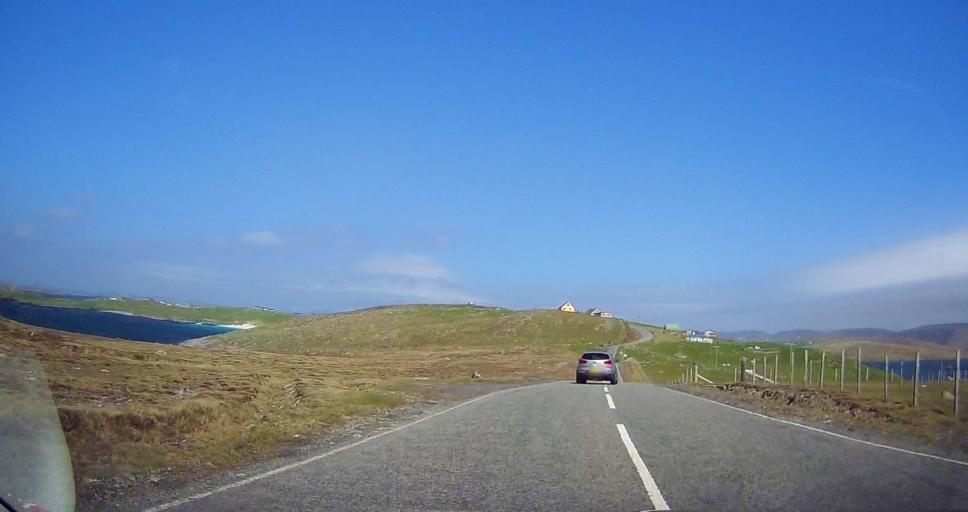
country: GB
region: Scotland
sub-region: Shetland Islands
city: Sandwick
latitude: 60.0920
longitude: -1.3244
